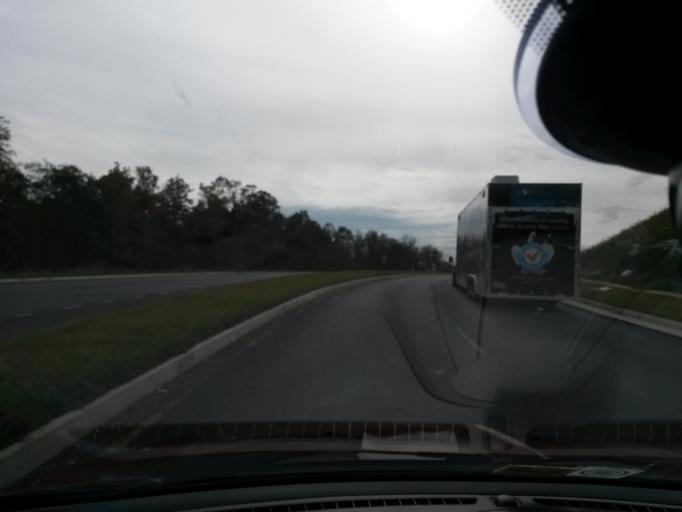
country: US
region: Virginia
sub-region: Botetourt County
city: Cloverdale
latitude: 37.3883
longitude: -79.8966
